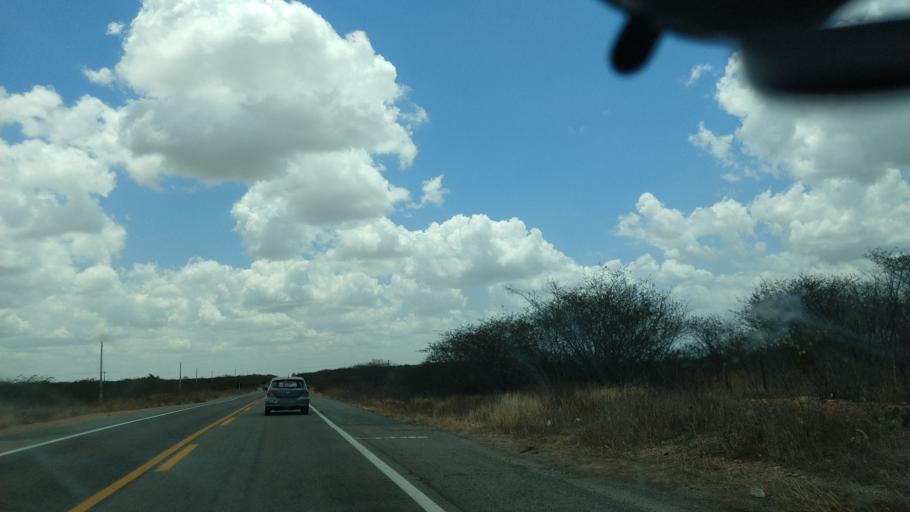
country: BR
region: Rio Grande do Norte
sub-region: Cerro Cora
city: Cerro Cora
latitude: -6.2072
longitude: -36.2837
